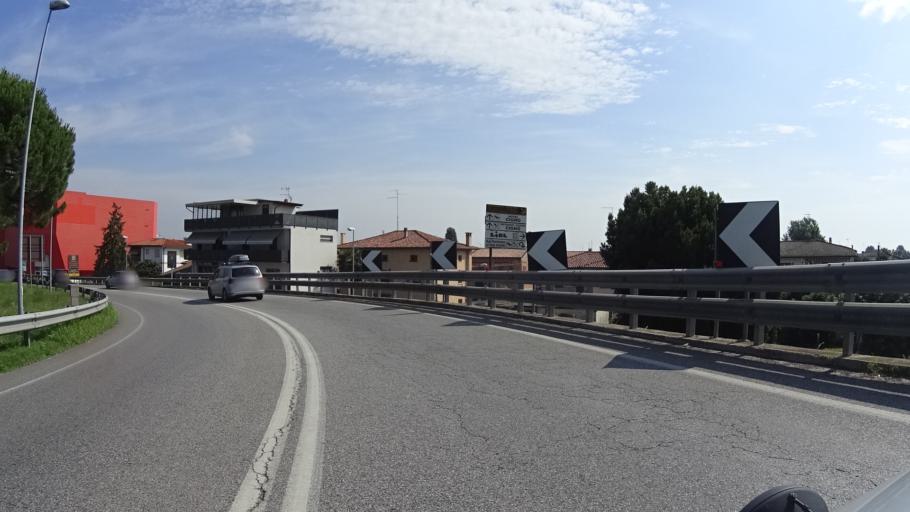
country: IT
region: Veneto
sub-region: Provincia di Venezia
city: San Michele al Tagliamento
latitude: 45.7707
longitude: 12.9983
